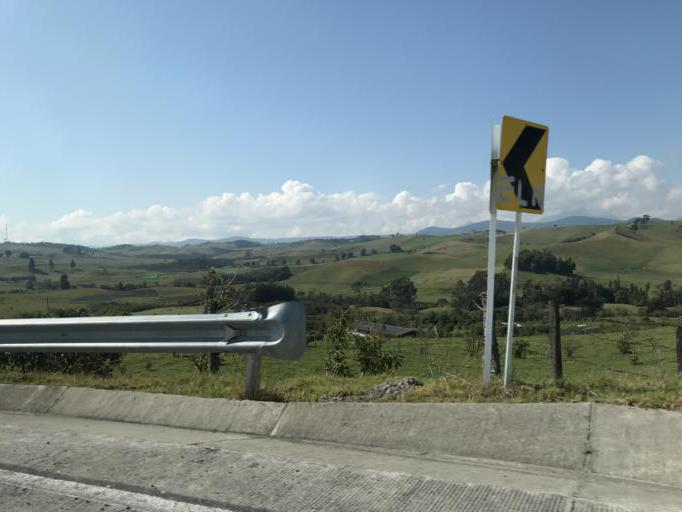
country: CO
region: Cauca
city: Paispamba
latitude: 2.2614
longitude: -76.5068
